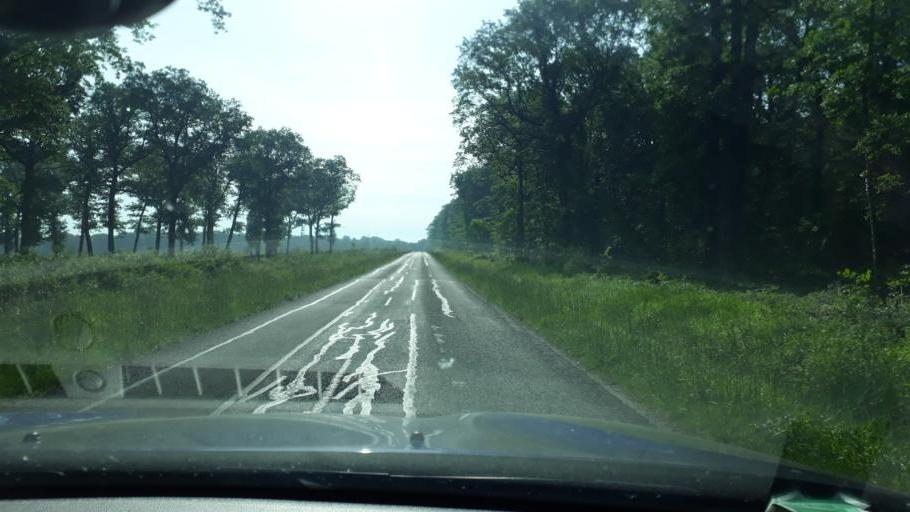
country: FR
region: Centre
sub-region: Departement du Loiret
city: Dadonville
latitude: 48.0604
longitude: 2.2424
